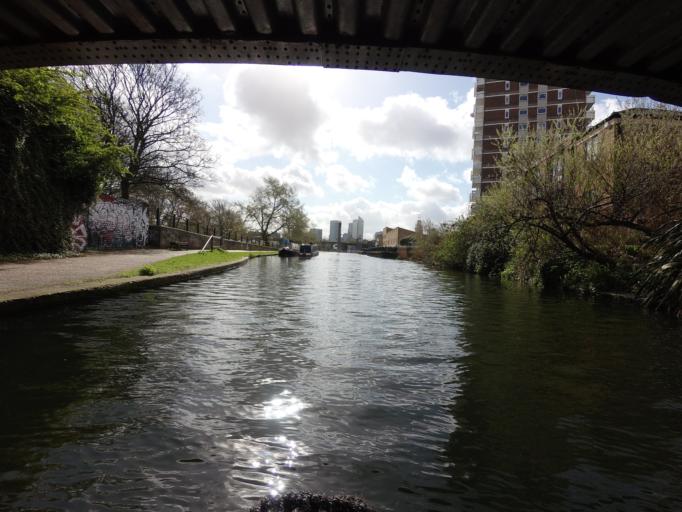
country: GB
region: England
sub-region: Greater London
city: Poplar
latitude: 51.5184
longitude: -0.0356
